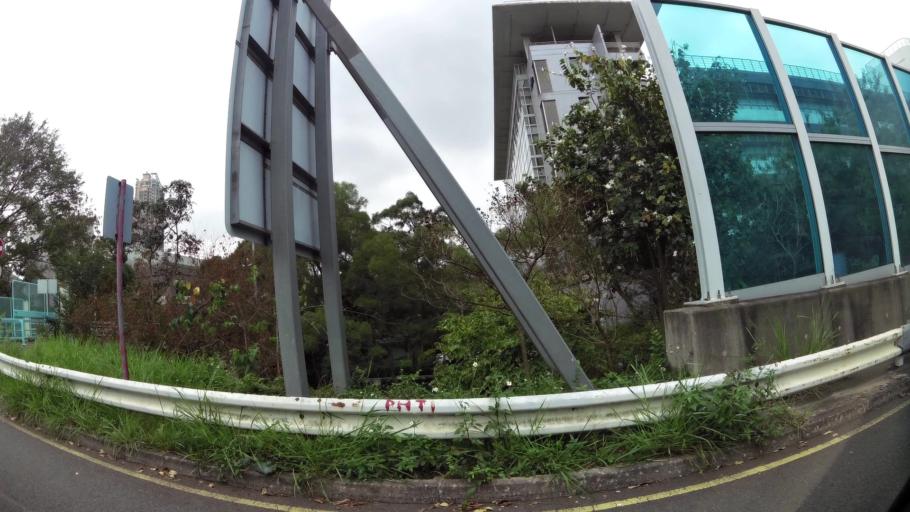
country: HK
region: Sha Tin
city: Sha Tin
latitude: 22.3906
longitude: 114.1973
